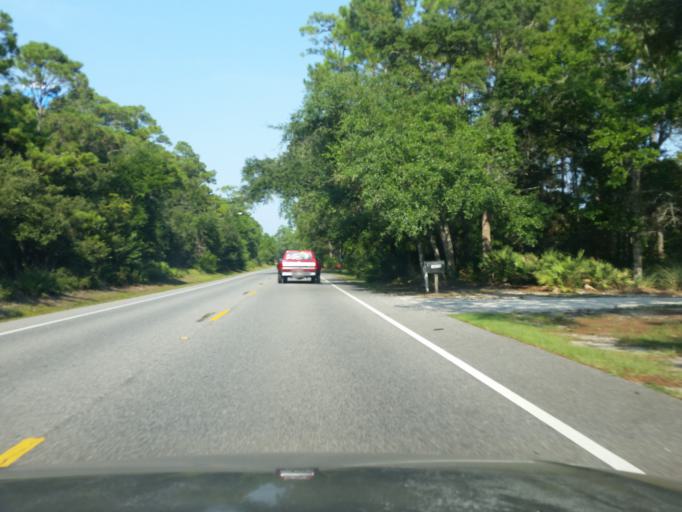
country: US
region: Alabama
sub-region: Baldwin County
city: Gulf Shores
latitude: 30.2465
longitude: -87.7801
